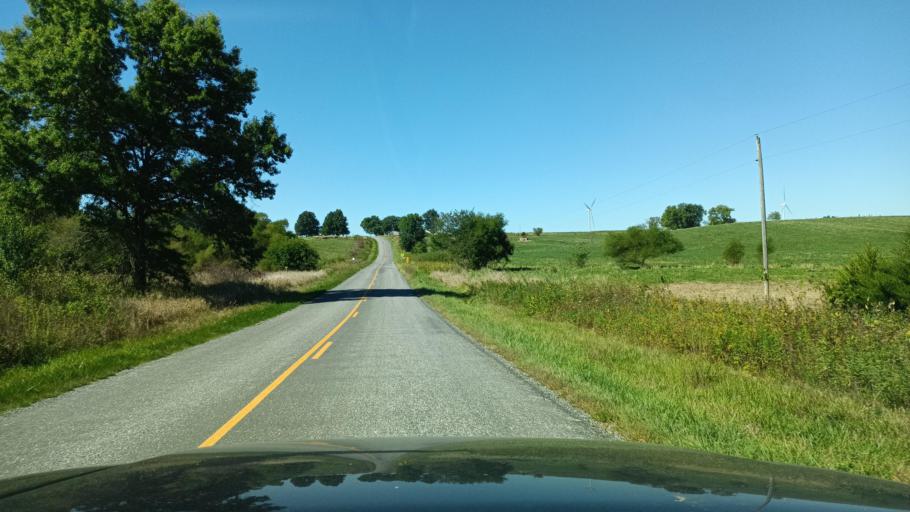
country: US
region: Missouri
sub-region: Adair County
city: Kirksville
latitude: 40.3308
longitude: -92.5096
